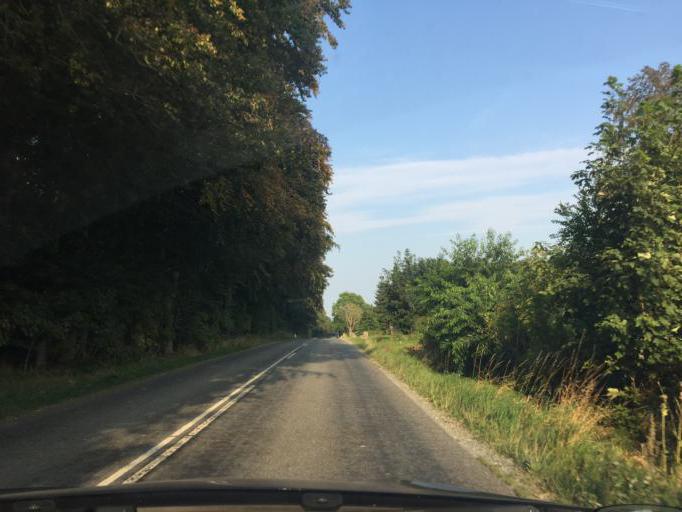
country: DK
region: South Denmark
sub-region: Faaborg-Midtfyn Kommune
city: Arslev
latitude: 55.2806
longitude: 10.5127
